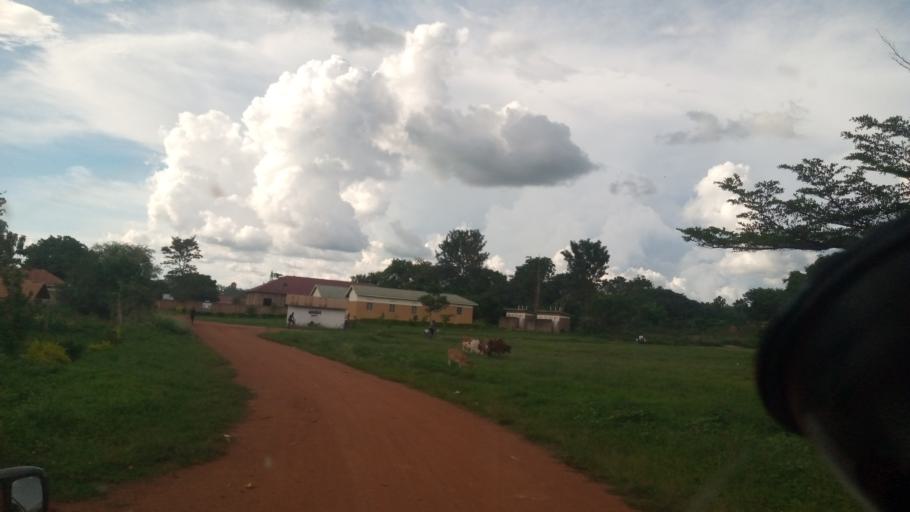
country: UG
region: Northern Region
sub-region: Lira District
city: Lira
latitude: 2.2397
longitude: 32.9008
